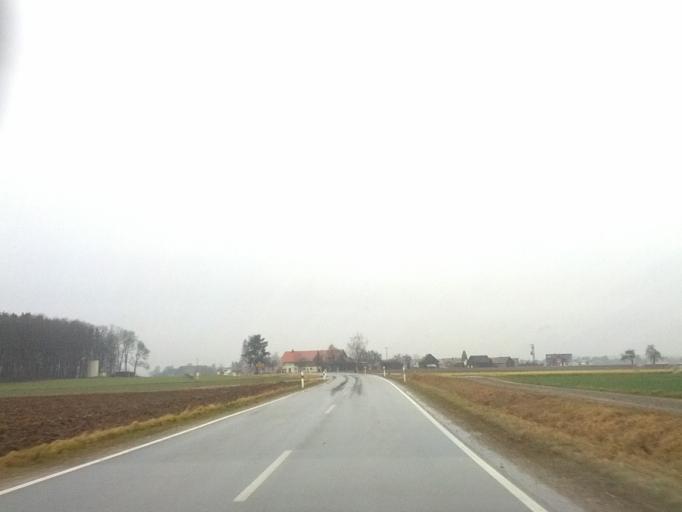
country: DE
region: Baden-Wuerttemberg
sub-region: Tuebingen Region
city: Erlenmoos
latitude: 48.0485
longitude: 9.9821
